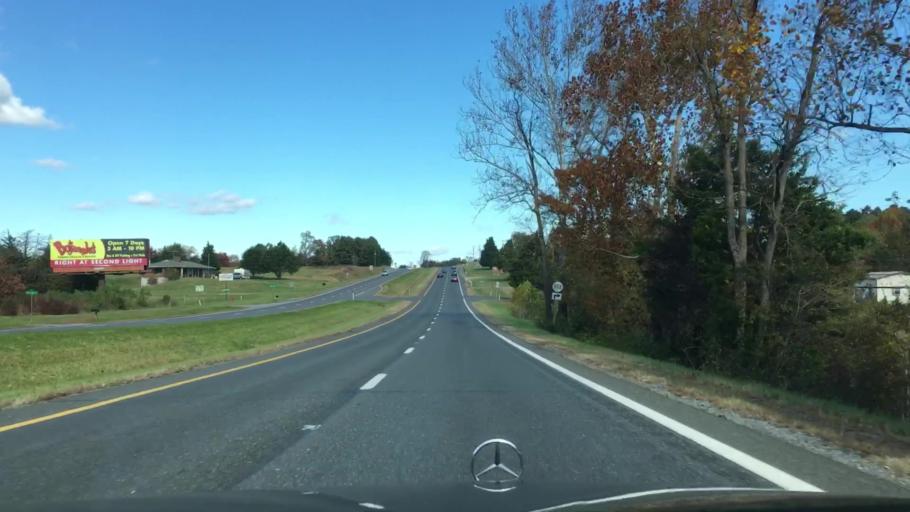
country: US
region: Virginia
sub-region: Campbell County
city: Altavista
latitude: 37.1806
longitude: -79.2049
